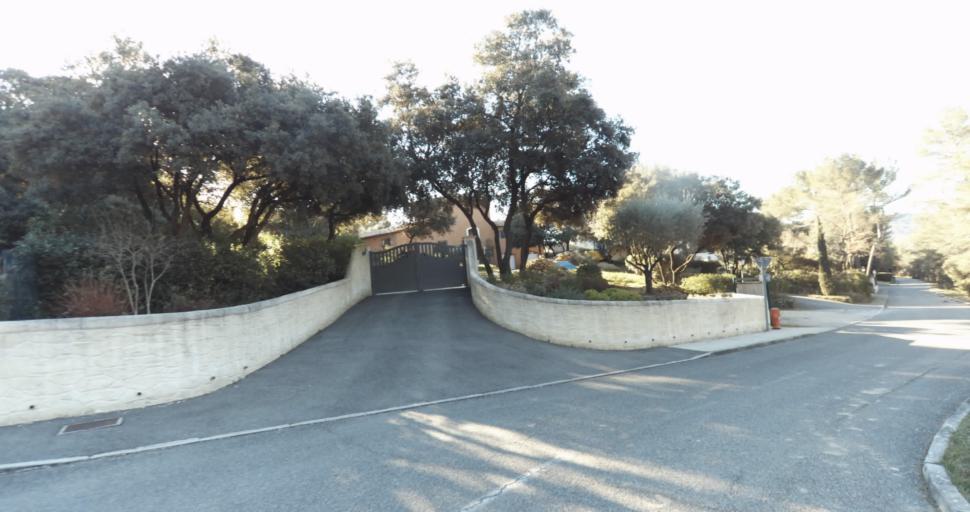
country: FR
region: Provence-Alpes-Cote d'Azur
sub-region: Departement des Bouches-du-Rhone
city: Peypin
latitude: 43.4052
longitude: 5.5730
